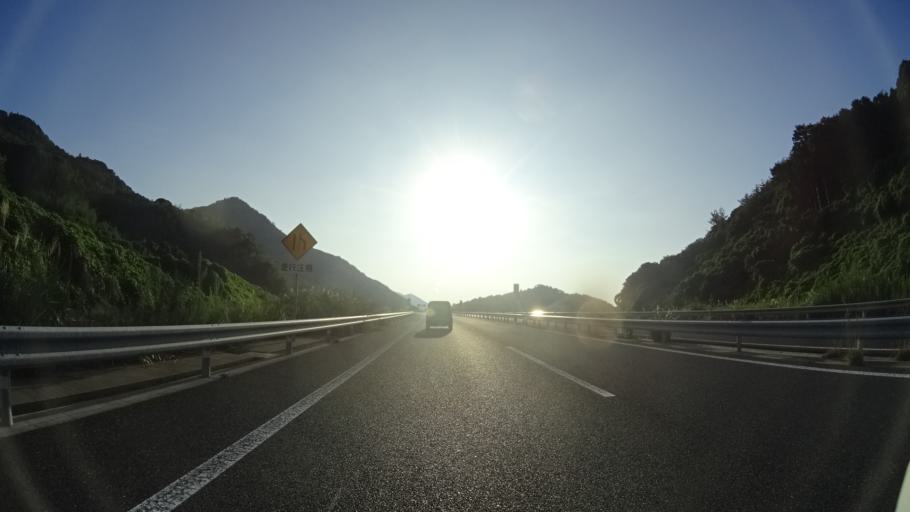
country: JP
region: Yamaguchi
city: Hagi
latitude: 34.3889
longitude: 131.3260
